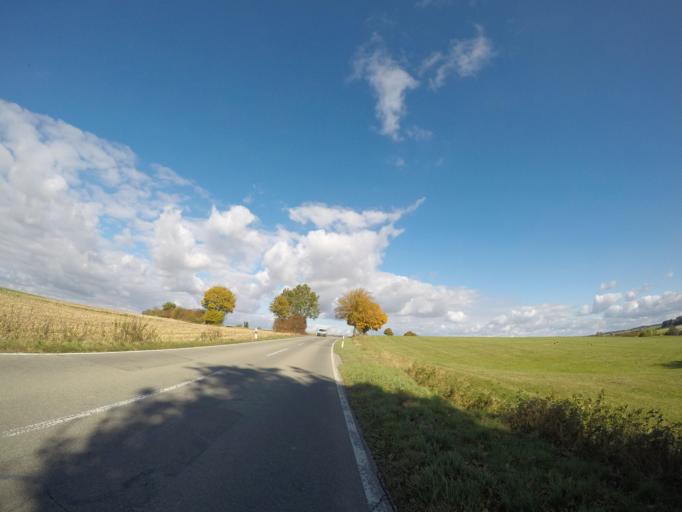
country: DE
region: Baden-Wuerttemberg
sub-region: Tuebingen Region
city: Grundsheim
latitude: 48.1591
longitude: 9.6744
